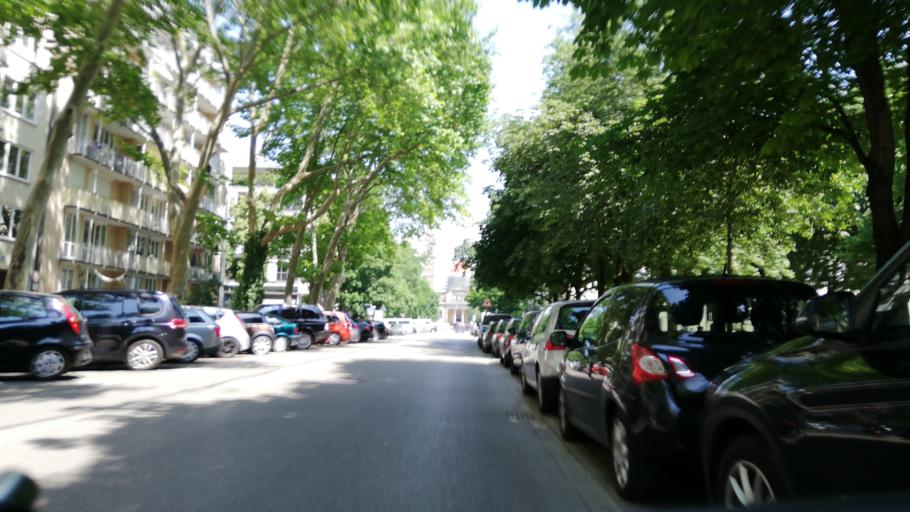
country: DE
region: Bavaria
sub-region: Upper Bavaria
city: Munich
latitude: 48.1582
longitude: 11.5799
